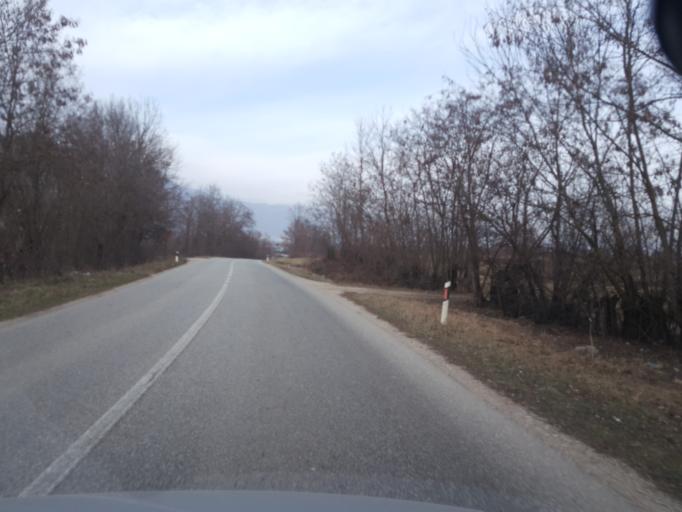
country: XK
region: Pec
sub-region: Komuna e Istogut
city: Istok
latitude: 42.7397
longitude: 20.4826
